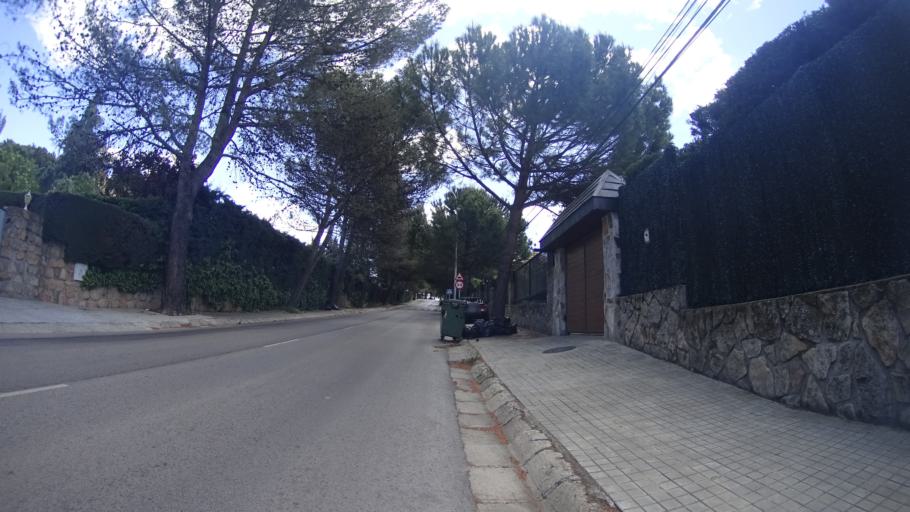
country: ES
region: Madrid
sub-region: Provincia de Madrid
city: Villaviciosa de Odon
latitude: 40.3723
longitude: -3.9267
